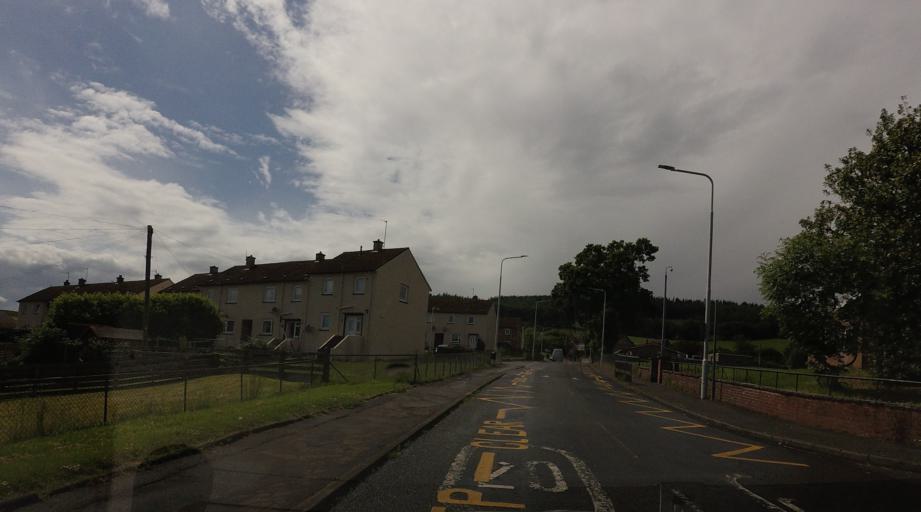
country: GB
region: Scotland
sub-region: Fife
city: Ballingry
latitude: 56.1637
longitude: -3.3327
